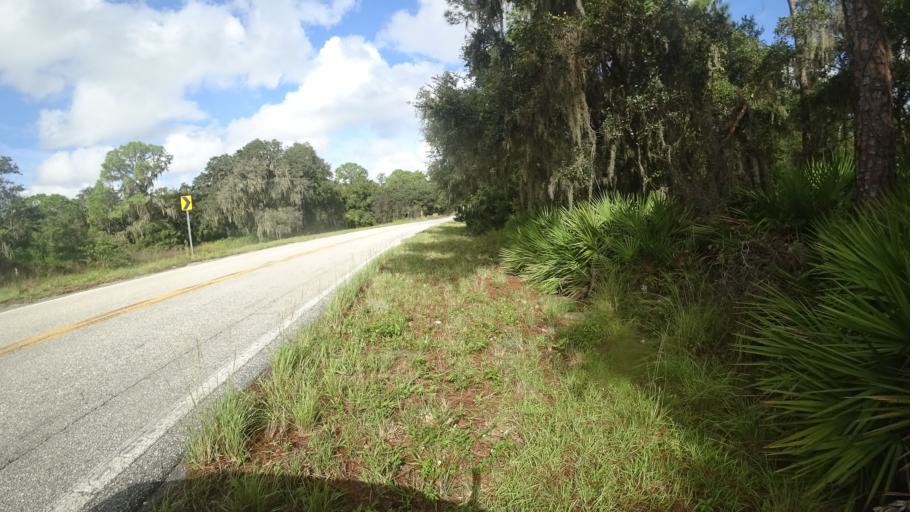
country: US
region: Florida
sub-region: Hillsborough County
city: Wimauma
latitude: 27.5383
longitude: -82.1029
